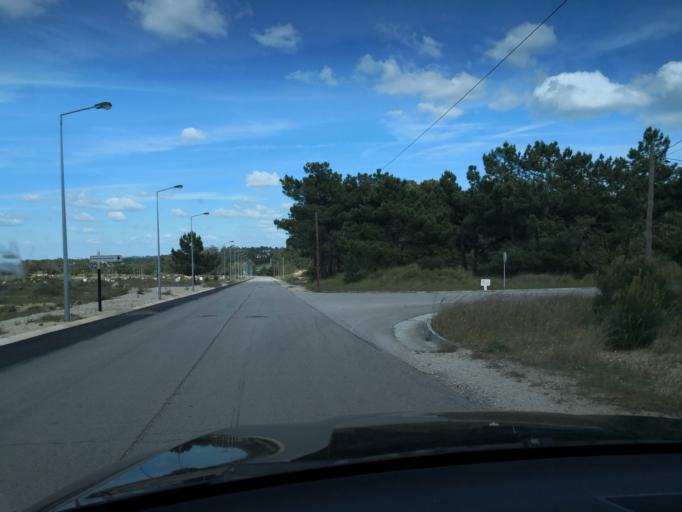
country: PT
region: Setubal
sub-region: Seixal
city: Aldeia de Paio Pires
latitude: 38.5462
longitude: -9.0471
